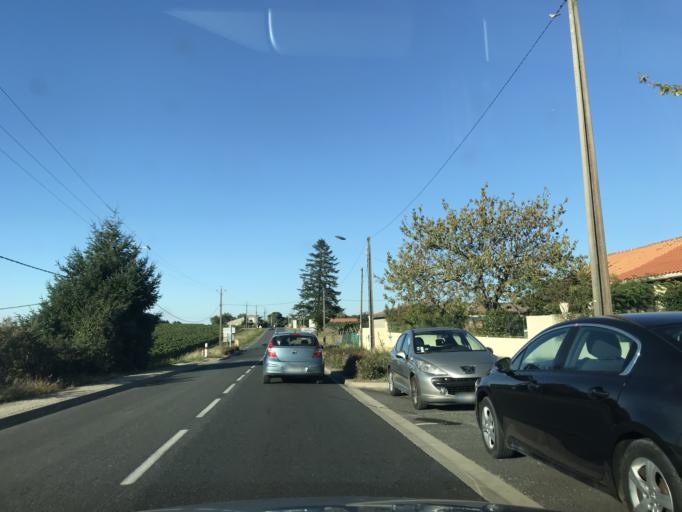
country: FR
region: Aquitaine
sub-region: Departement de la Gironde
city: Saint-Macaire
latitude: 44.5870
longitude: -0.2116
